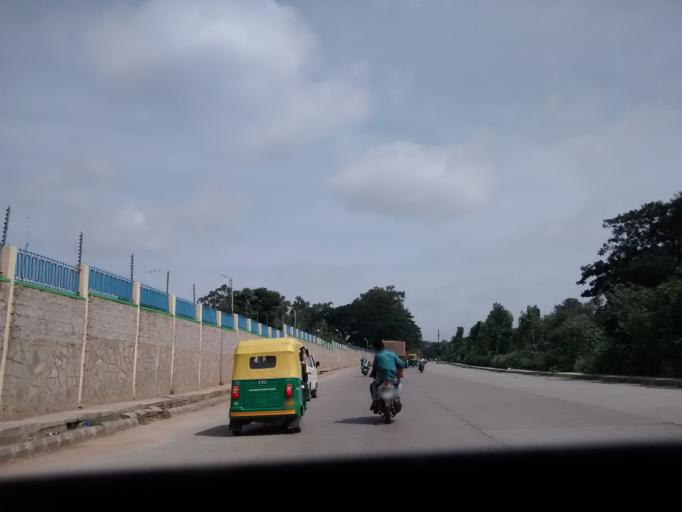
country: IN
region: Karnataka
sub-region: Bangalore Urban
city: Bangalore
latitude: 12.9800
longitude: 77.6516
